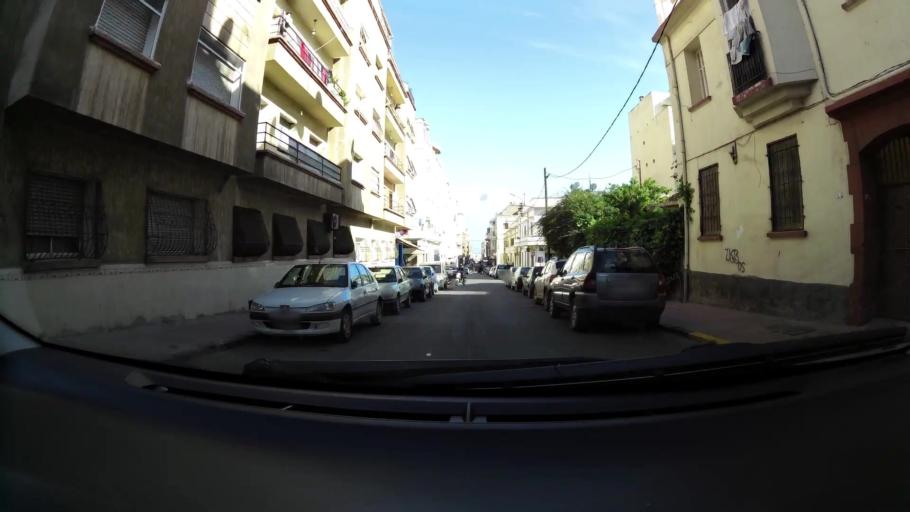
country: MA
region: Grand Casablanca
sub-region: Casablanca
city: Casablanca
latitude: 33.5989
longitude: -7.5806
